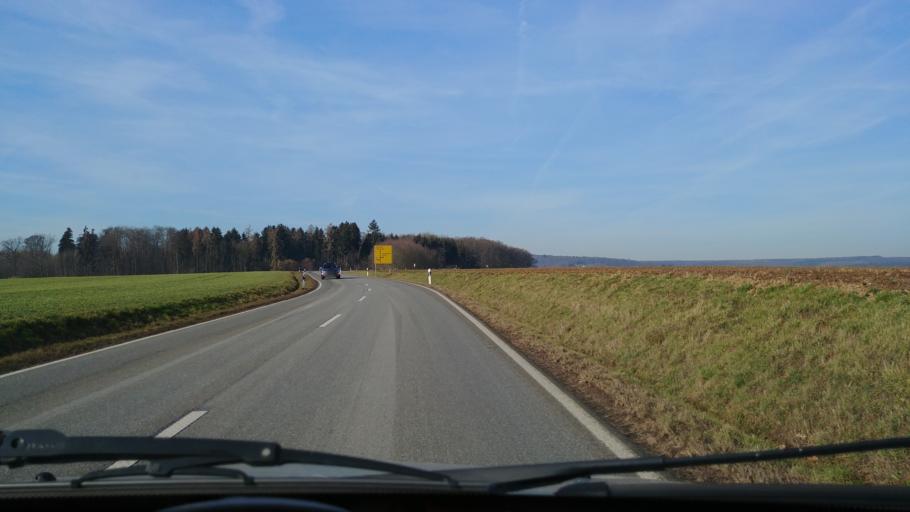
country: DE
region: Rheinland-Pfalz
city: Ehr
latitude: 50.2448
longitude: 7.7852
